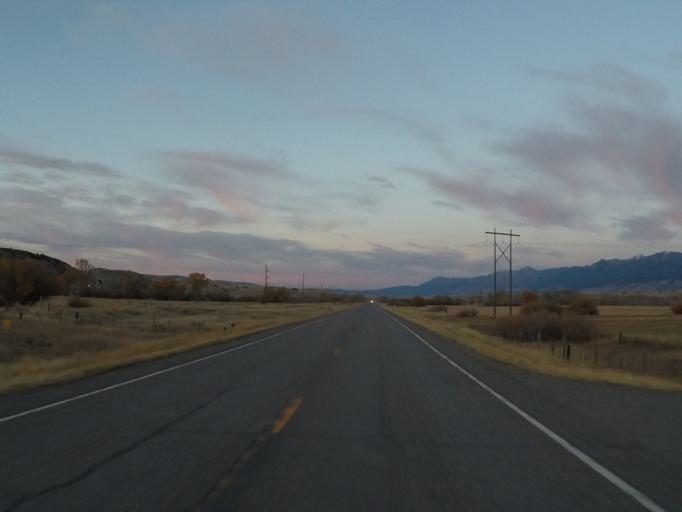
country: US
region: Montana
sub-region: Park County
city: Livingston
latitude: 45.3556
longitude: -110.7463
